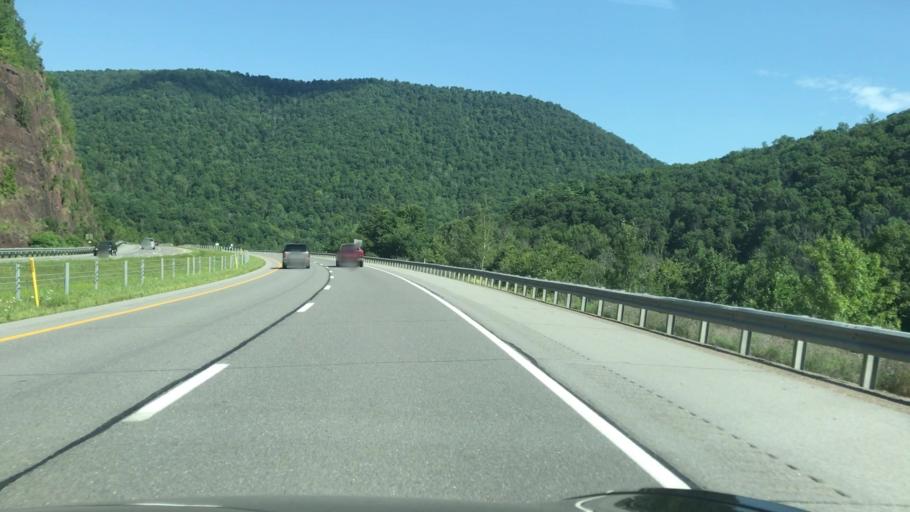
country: US
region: Pennsylvania
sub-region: Lycoming County
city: Garden View
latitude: 41.3434
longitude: -77.0897
